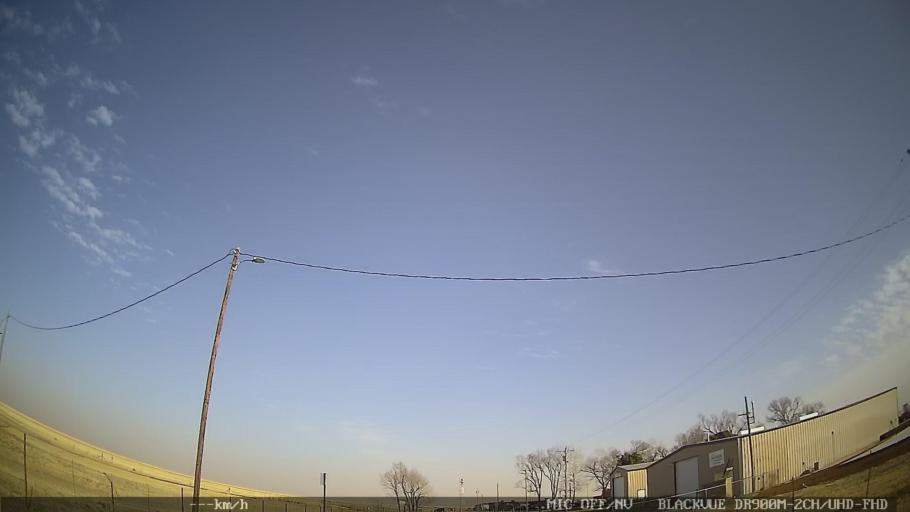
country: US
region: New Mexico
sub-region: Curry County
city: Texico
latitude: 34.4271
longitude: -103.0889
